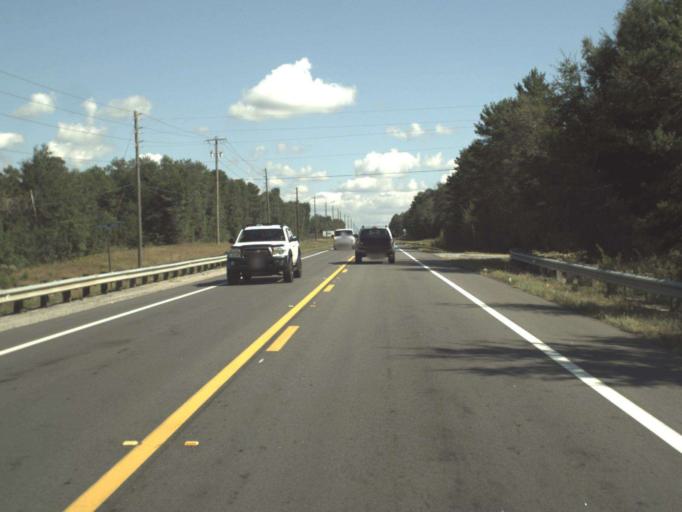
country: US
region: Florida
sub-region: Walton County
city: Freeport
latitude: 30.5114
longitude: -86.1753
